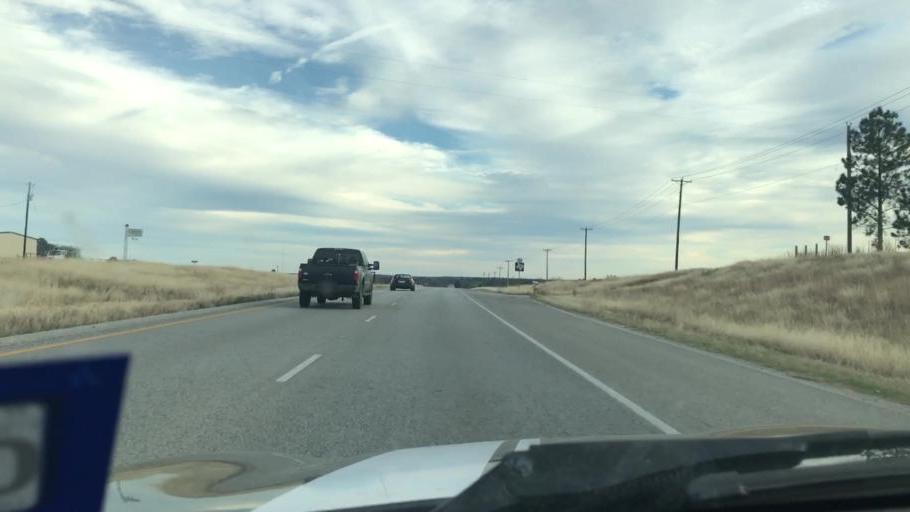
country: US
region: Texas
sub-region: Bastrop County
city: Elgin
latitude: 30.3137
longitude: -97.3091
